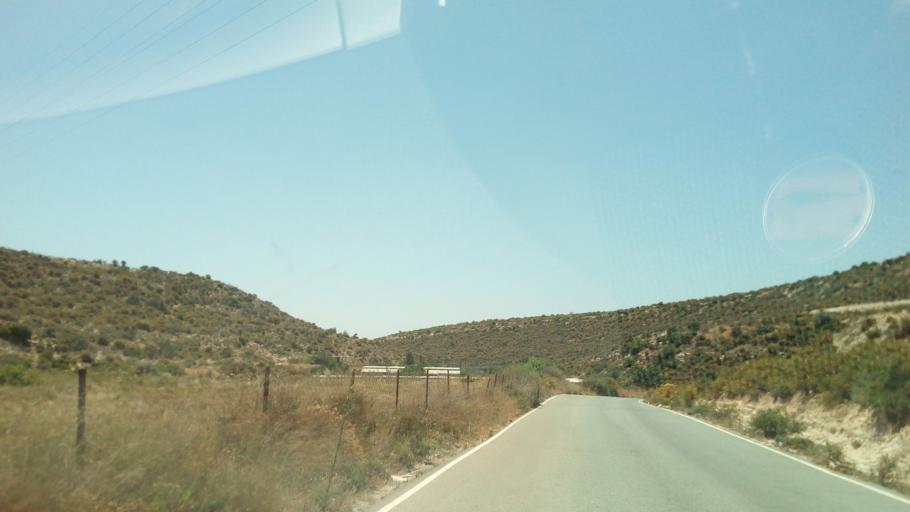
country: CY
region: Limassol
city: Ypsonas
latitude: 34.7204
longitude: 32.9533
